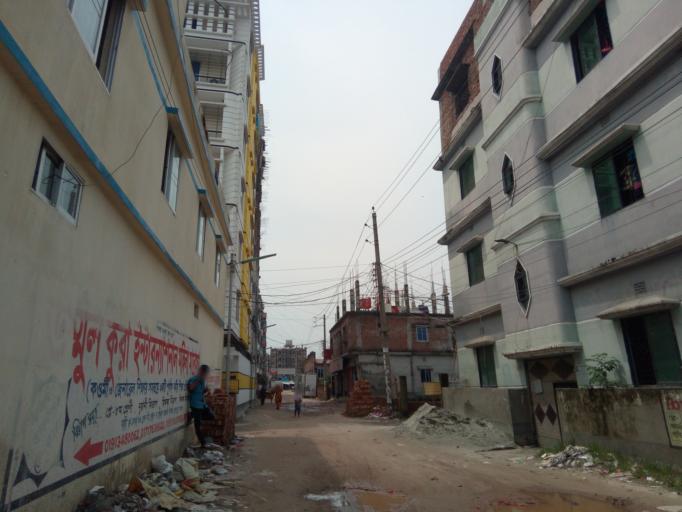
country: BD
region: Dhaka
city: Azimpur
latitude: 23.7440
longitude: 90.3493
